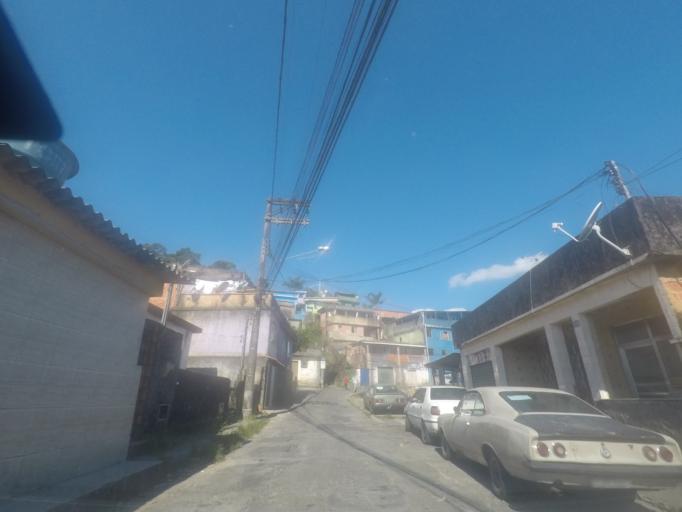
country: BR
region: Rio de Janeiro
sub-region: Petropolis
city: Petropolis
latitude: -22.5456
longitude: -43.2021
